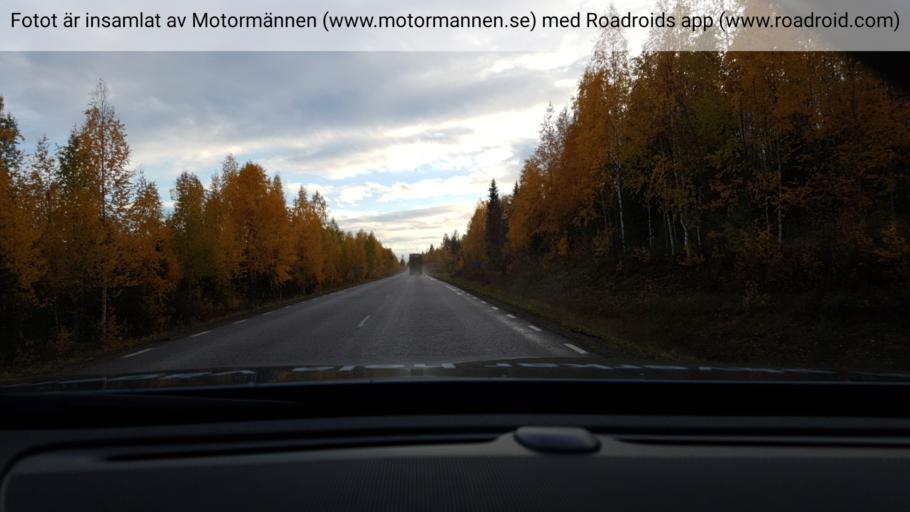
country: SE
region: Norrbotten
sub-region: Overkalix Kommun
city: OEverkalix
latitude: 66.8207
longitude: 22.7477
